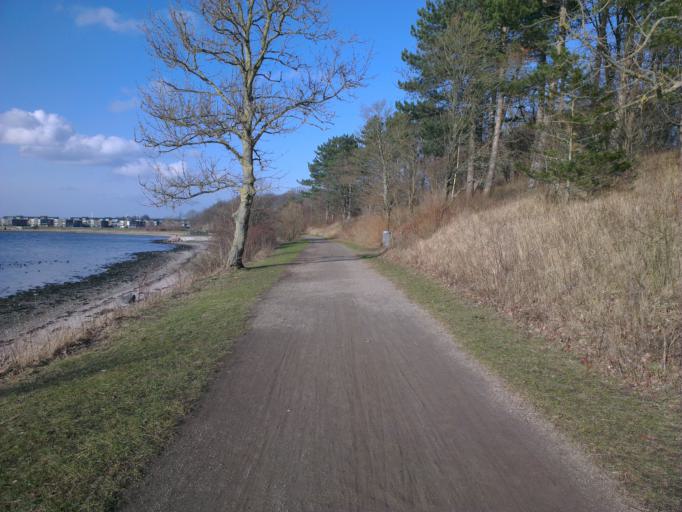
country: DK
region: Capital Region
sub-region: Frederikssund Kommune
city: Frederikssund
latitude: 55.8296
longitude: 12.0575
